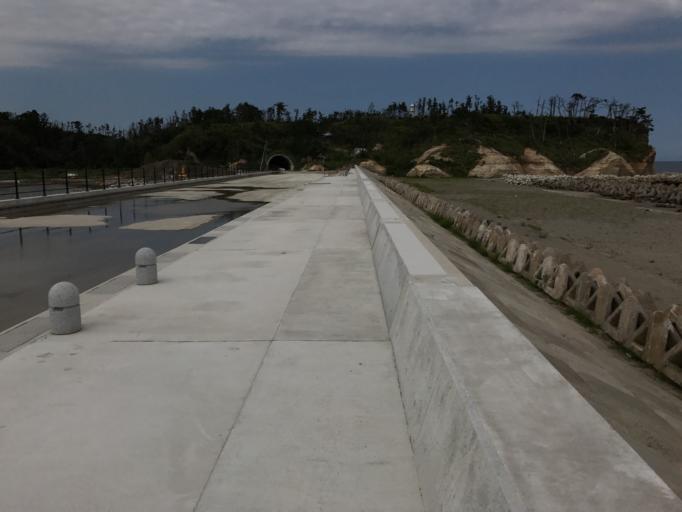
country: JP
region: Miyagi
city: Marumori
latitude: 37.8204
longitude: 140.9857
